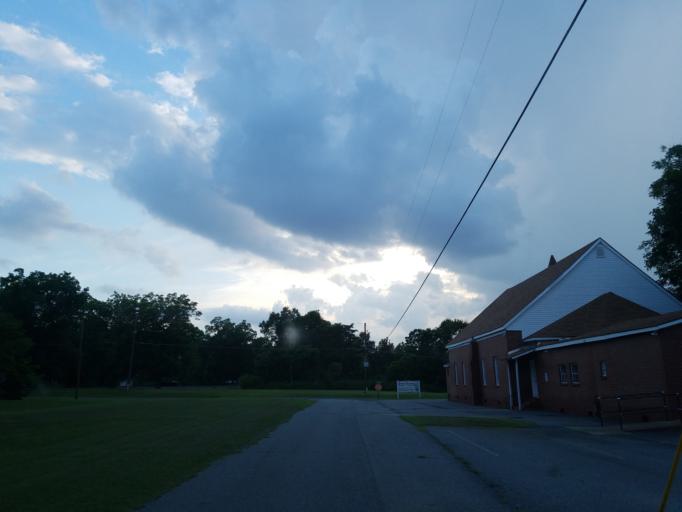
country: US
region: Georgia
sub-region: Dooly County
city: Unadilla
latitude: 32.1915
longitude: -83.7593
